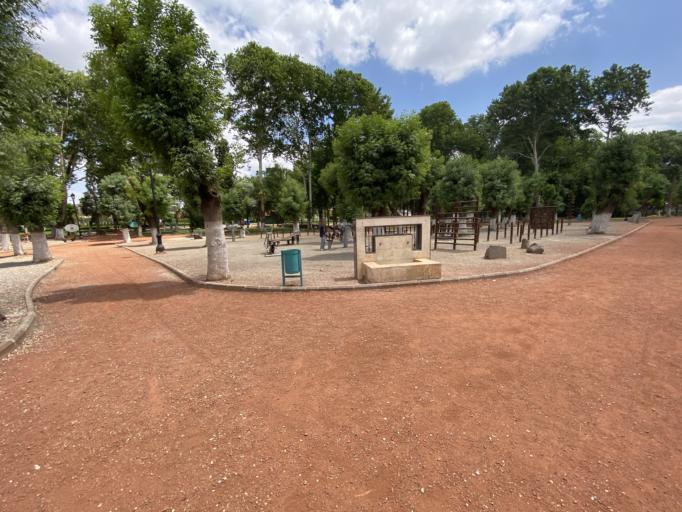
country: TR
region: Gaziantep
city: Sahinbey
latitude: 37.0617
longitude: 37.3534
